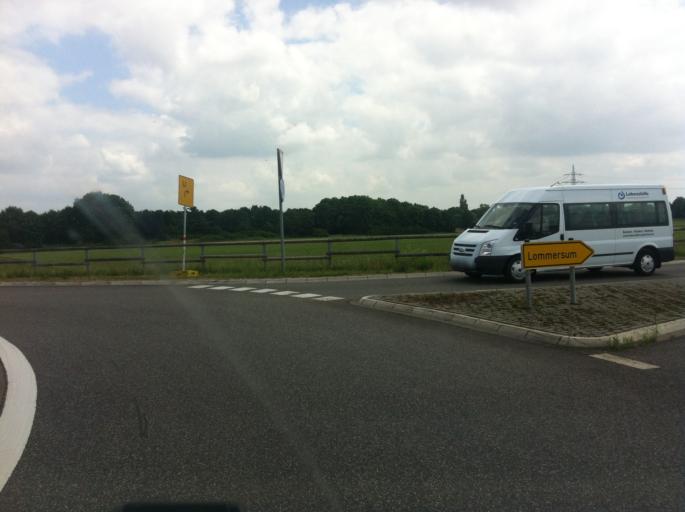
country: DE
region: North Rhine-Westphalia
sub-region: Regierungsbezirk Koln
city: Weilerswist
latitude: 50.7487
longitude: 6.8271
